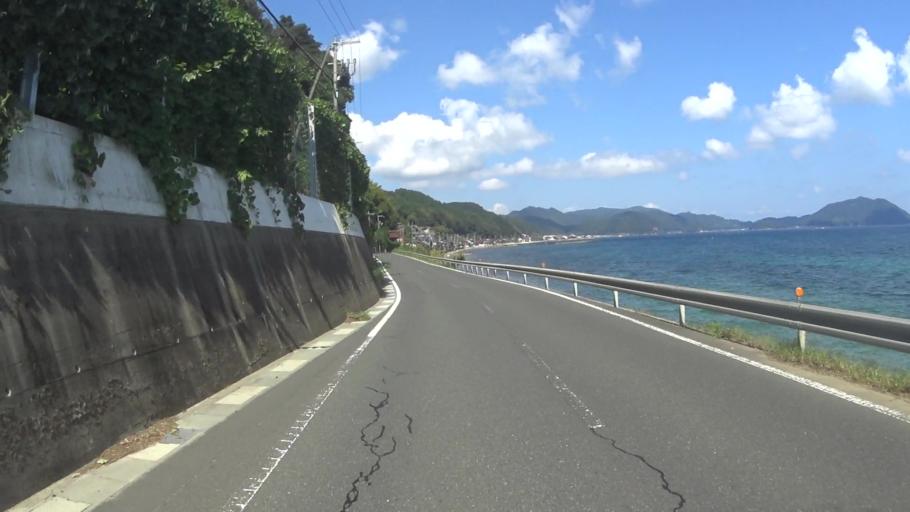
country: JP
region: Kyoto
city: Miyazu
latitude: 35.6438
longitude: 135.2507
